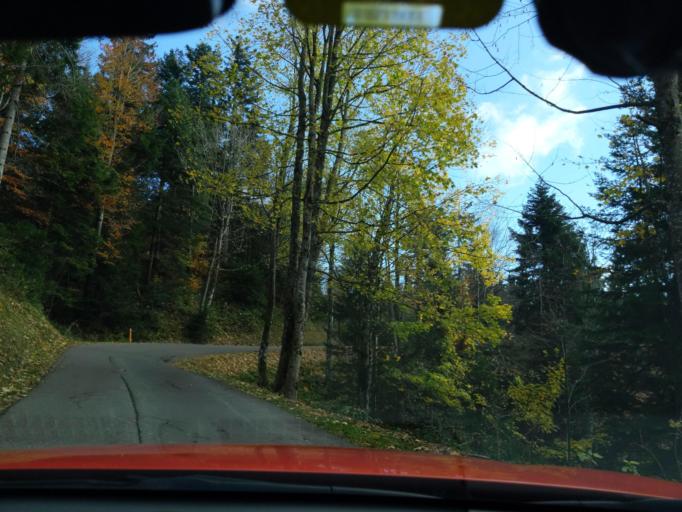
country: AT
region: Vorarlberg
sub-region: Politischer Bezirk Bregenz
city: Eichenberg
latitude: 47.5401
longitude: 9.7989
